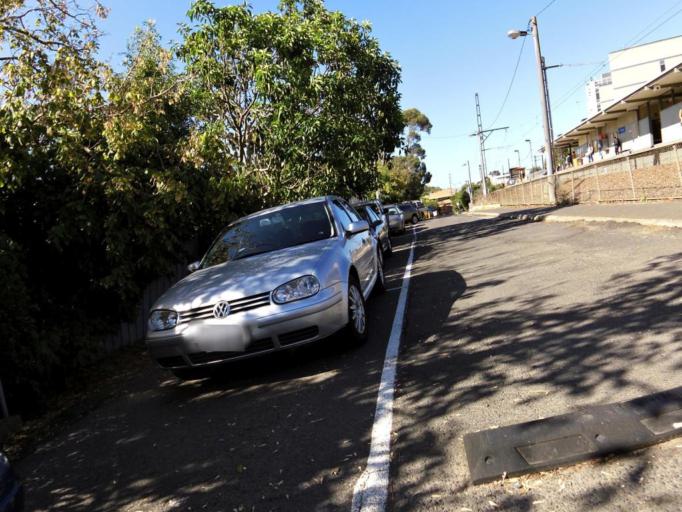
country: AU
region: Victoria
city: Ashburton
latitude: -37.8745
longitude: 145.0897
